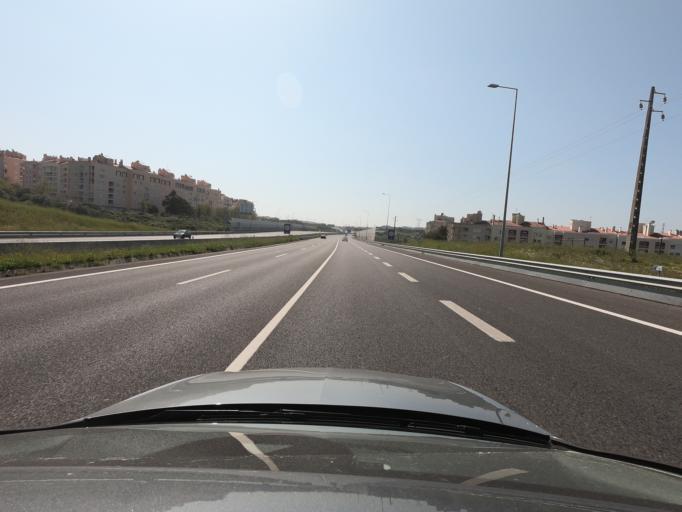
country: PT
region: Lisbon
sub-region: Sintra
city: Cacem
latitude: 38.7775
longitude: -9.2850
